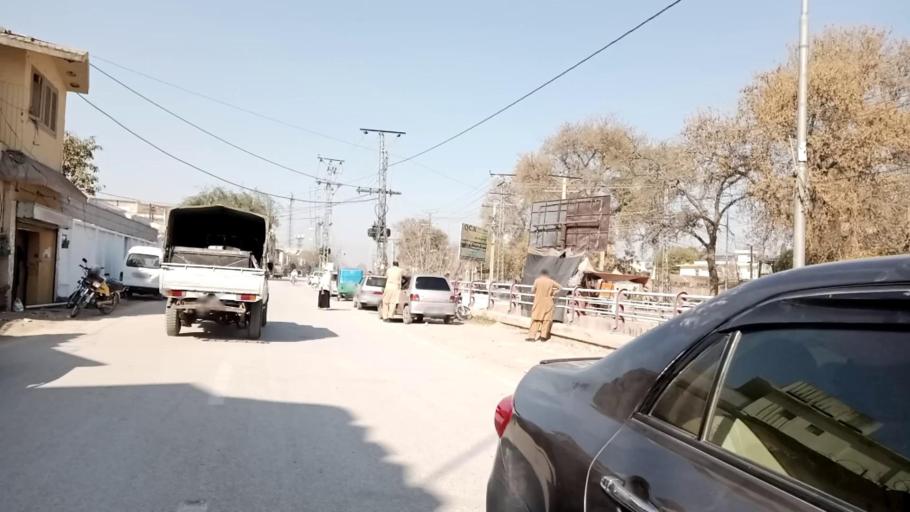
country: PK
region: Khyber Pakhtunkhwa
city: Peshawar
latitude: 33.9893
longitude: 71.4883
